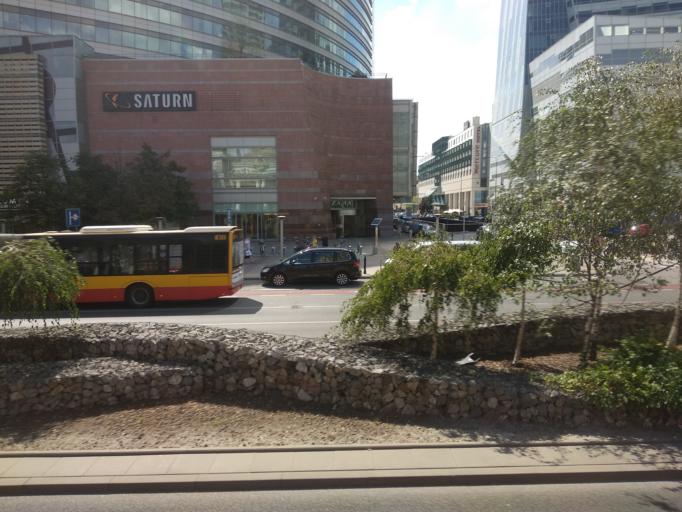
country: PL
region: Masovian Voivodeship
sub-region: Warszawa
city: Warsaw
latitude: 52.2310
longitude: 21.0041
